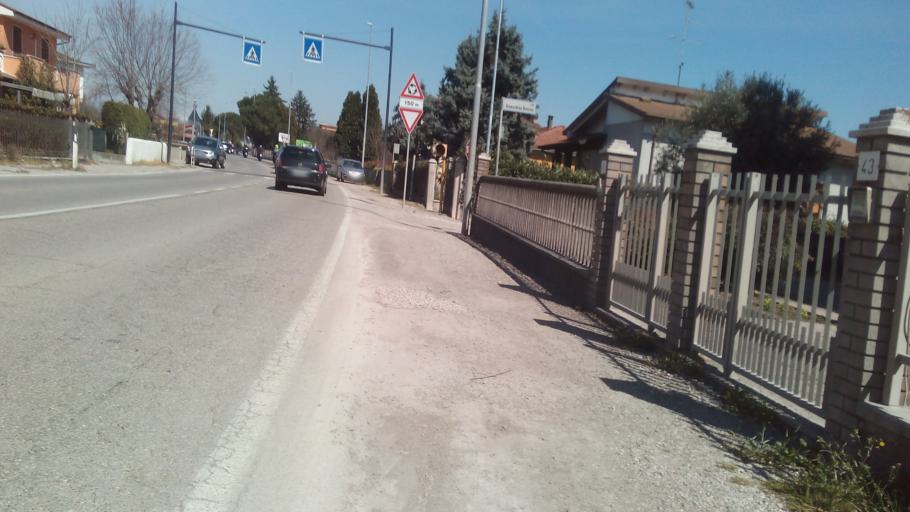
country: IT
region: Lombardy
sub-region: Provincia di Mantova
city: Goito
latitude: 45.2496
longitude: 10.6660
